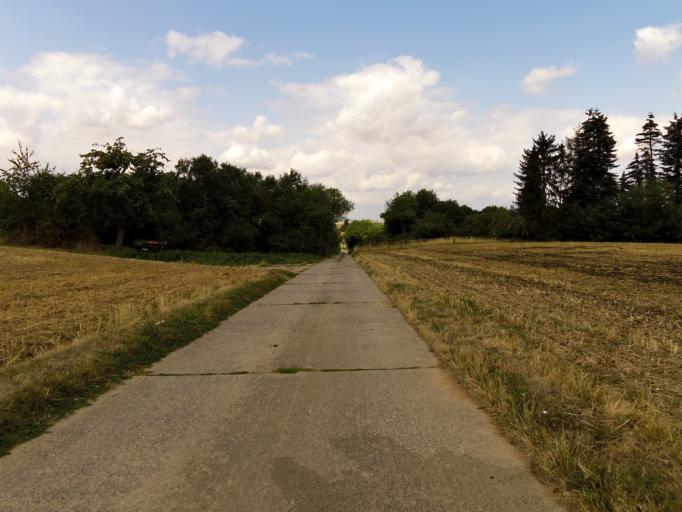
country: DE
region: Hesse
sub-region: Regierungsbezirk Darmstadt
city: Brensbach
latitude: 49.7702
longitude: 8.8865
